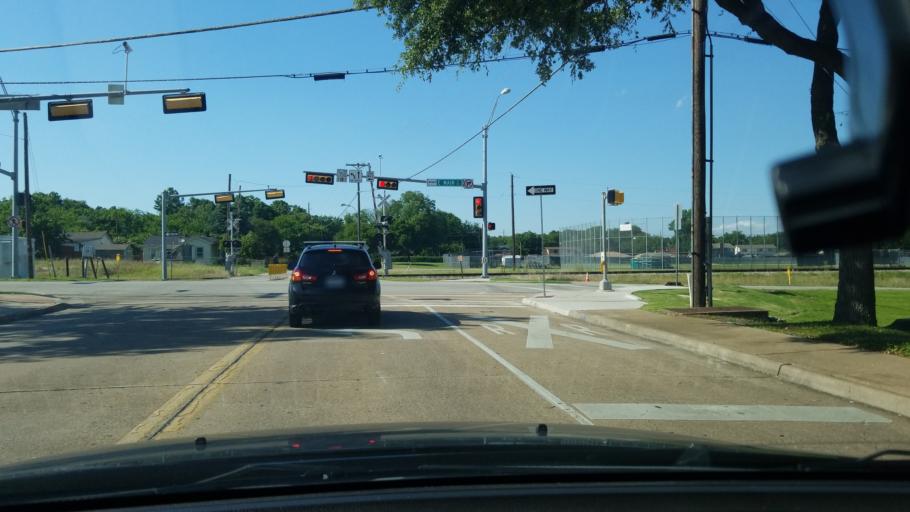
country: US
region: Texas
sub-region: Dallas County
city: Mesquite
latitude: 32.7665
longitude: -96.5941
